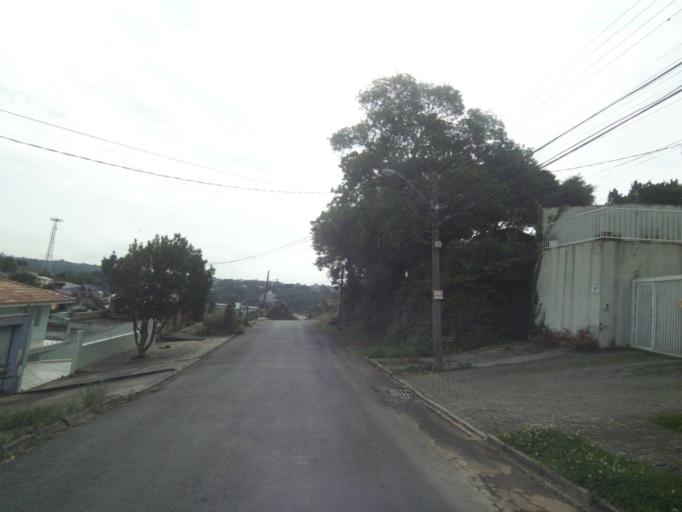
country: BR
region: Parana
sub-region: Curitiba
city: Curitiba
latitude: -25.4092
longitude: -49.3003
